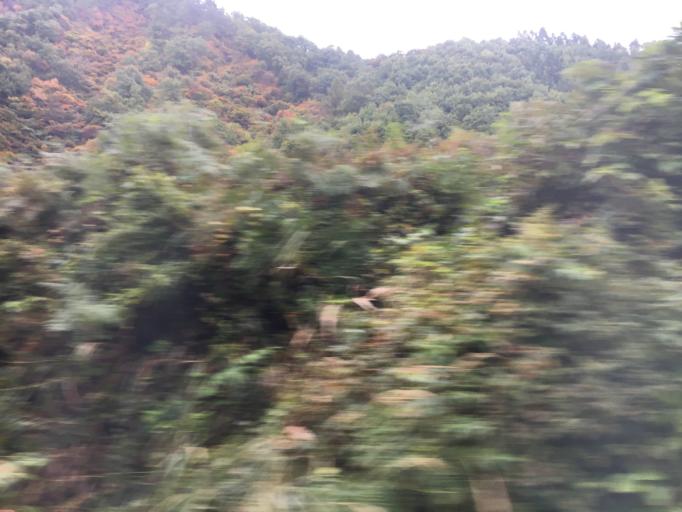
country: JP
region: Yamagata
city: Nagai
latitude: 38.0196
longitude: 139.8896
